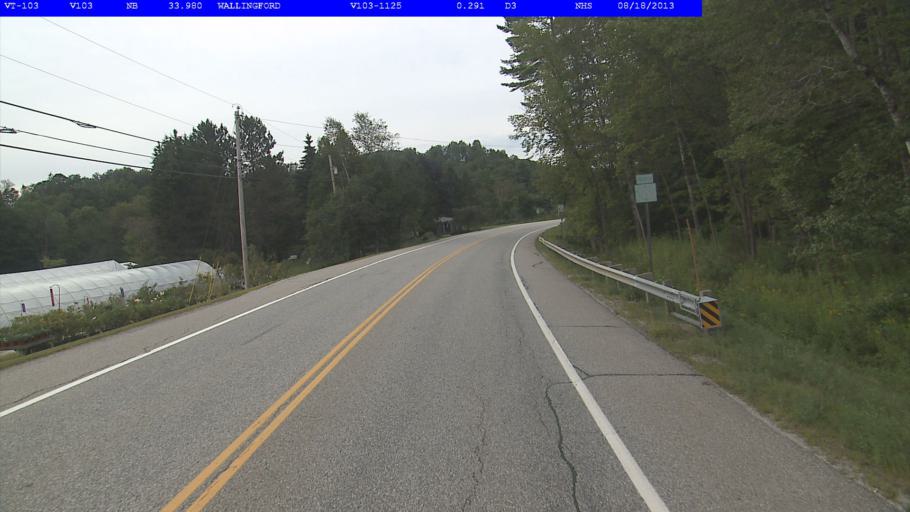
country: US
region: Vermont
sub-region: Rutland County
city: Rutland
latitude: 43.4510
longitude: -72.8776
